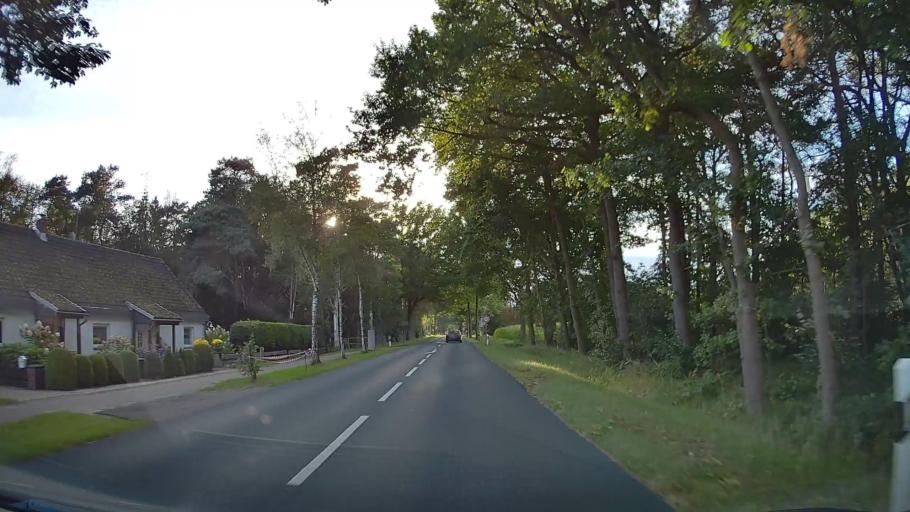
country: DE
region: Lower Saxony
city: Ottersberg
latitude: 53.0719
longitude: 9.1797
